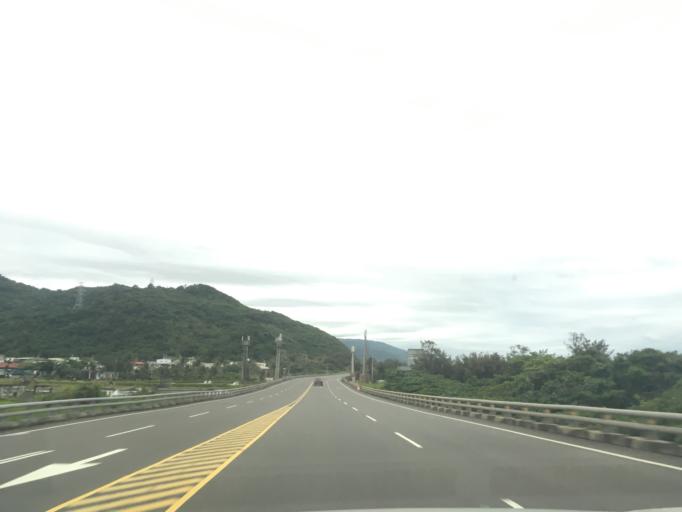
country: TW
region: Taiwan
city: Hengchun
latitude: 22.3055
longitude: 120.8899
